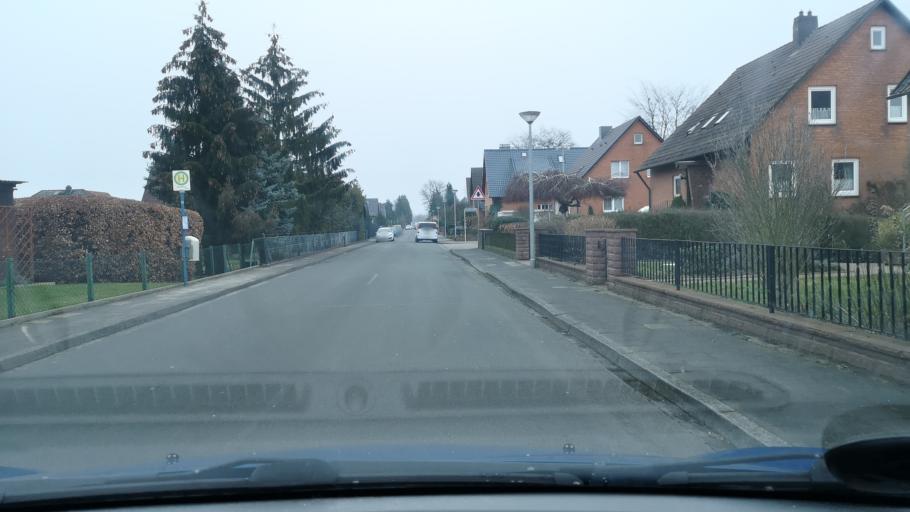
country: DE
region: Lower Saxony
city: Celle
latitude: 52.6045
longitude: 10.0632
